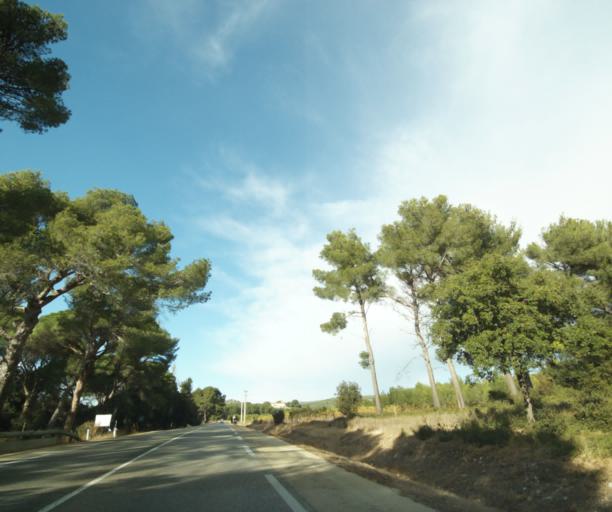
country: FR
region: Provence-Alpes-Cote d'Azur
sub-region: Departement des Bouches-du-Rhone
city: Sausset-les-Pins
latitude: 43.3569
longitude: 5.1023
